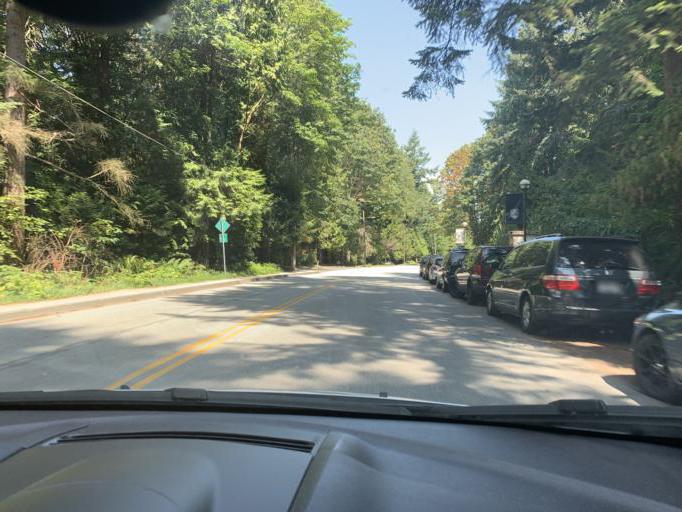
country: CA
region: British Columbia
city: West End
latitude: 49.2667
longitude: -123.2602
